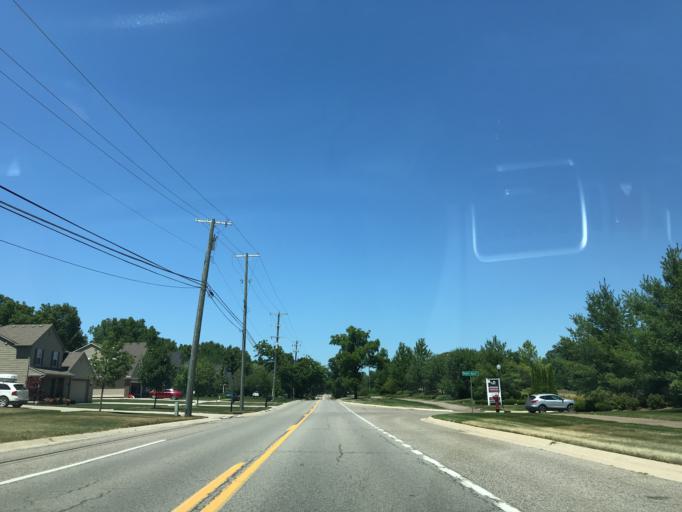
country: US
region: Michigan
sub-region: Oakland County
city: South Lyon
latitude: 42.4647
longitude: -83.6369
